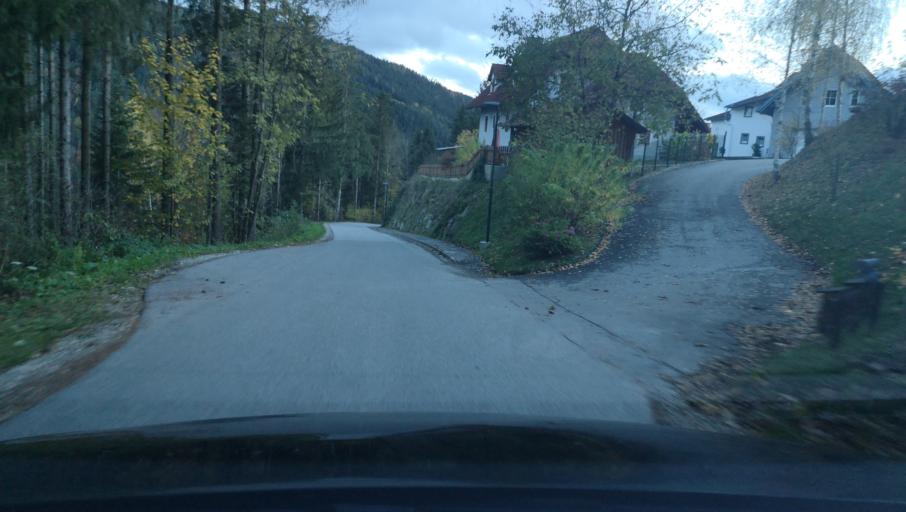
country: AT
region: Styria
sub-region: Politischer Bezirk Weiz
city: Koglhof
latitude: 47.3218
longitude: 15.6906
